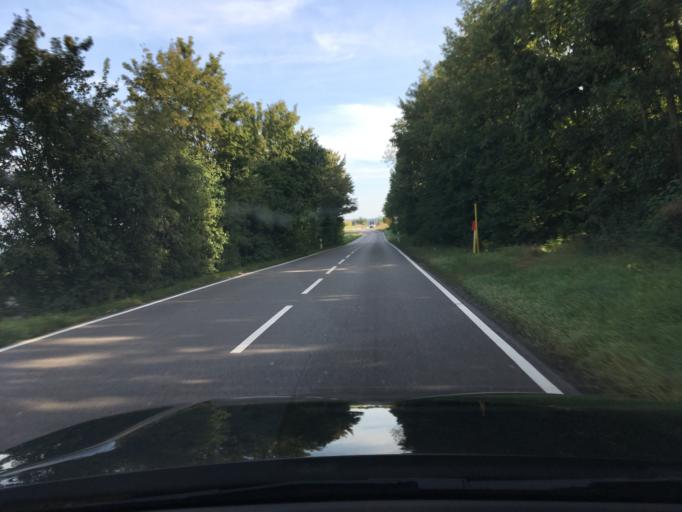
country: DE
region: Baden-Wuerttemberg
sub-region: Regierungsbezirk Stuttgart
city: Affalterbach
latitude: 48.9186
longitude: 9.3316
